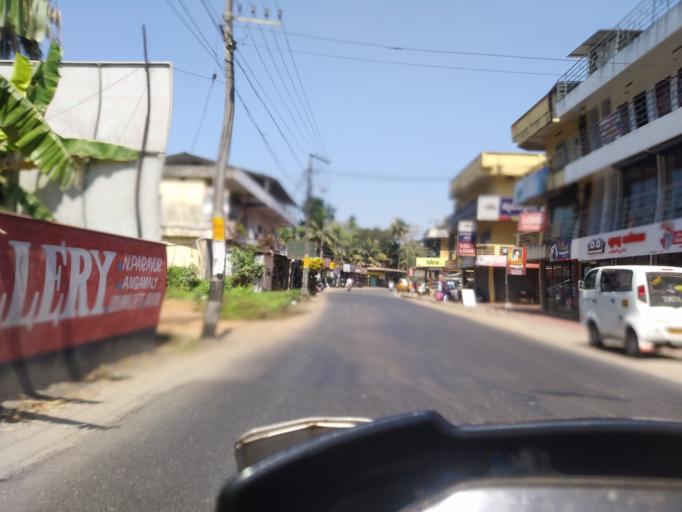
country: IN
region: Kerala
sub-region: Thrissur District
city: Kodungallur
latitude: 10.1712
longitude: 76.2120
